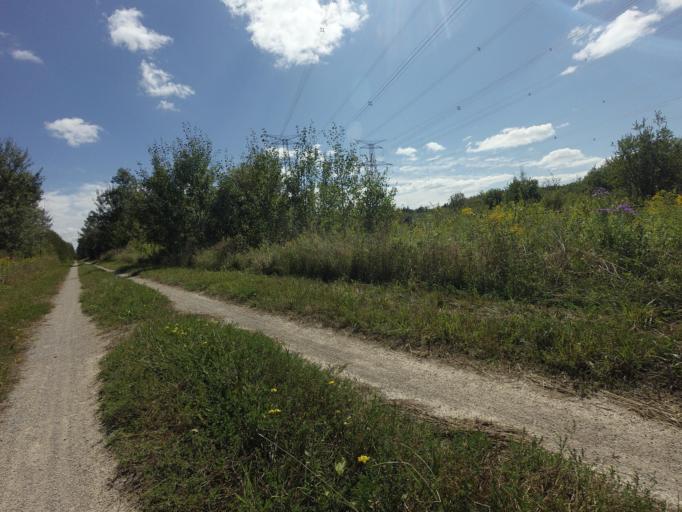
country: CA
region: Ontario
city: Orangeville
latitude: 43.7796
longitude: -80.2135
